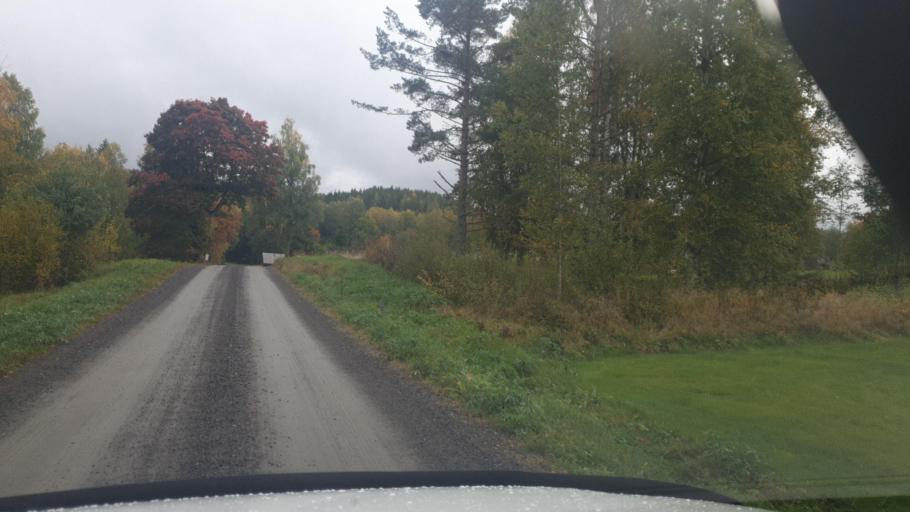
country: SE
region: Vaermland
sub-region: Torsby Kommun
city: Torsby
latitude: 59.9364
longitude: 12.8167
